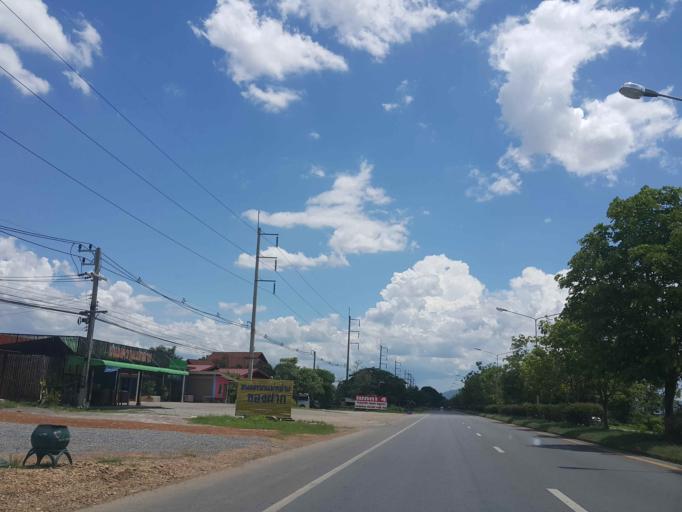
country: TH
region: Phrae
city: Nong Muang Khai
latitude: 18.2256
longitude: 100.2045
